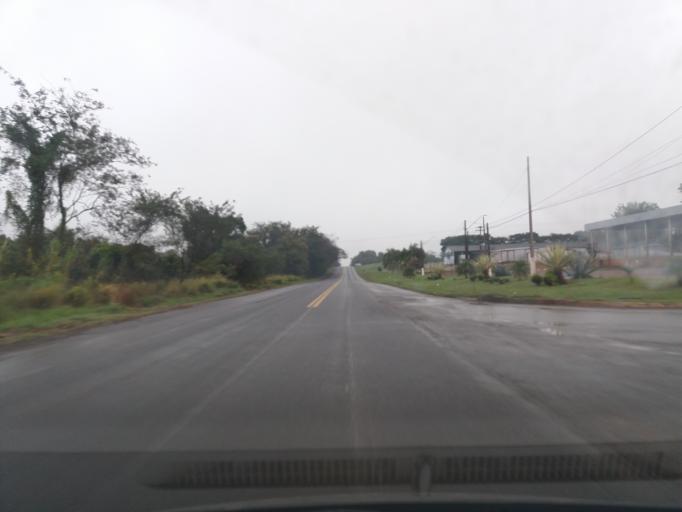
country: BR
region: Parana
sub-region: Ampere
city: Ampere
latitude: -25.8898
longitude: -53.4641
